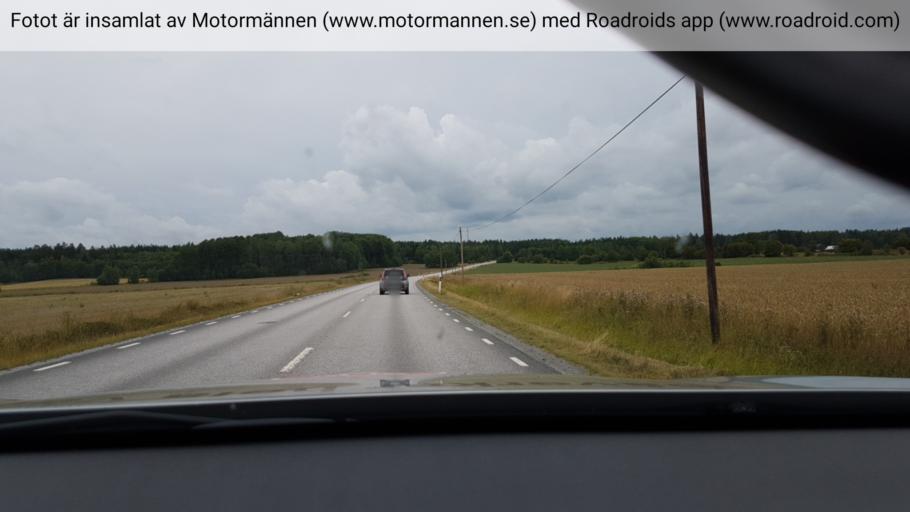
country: SE
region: Stockholm
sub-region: Vallentuna Kommun
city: Vallentuna
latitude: 59.7171
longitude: 18.0550
